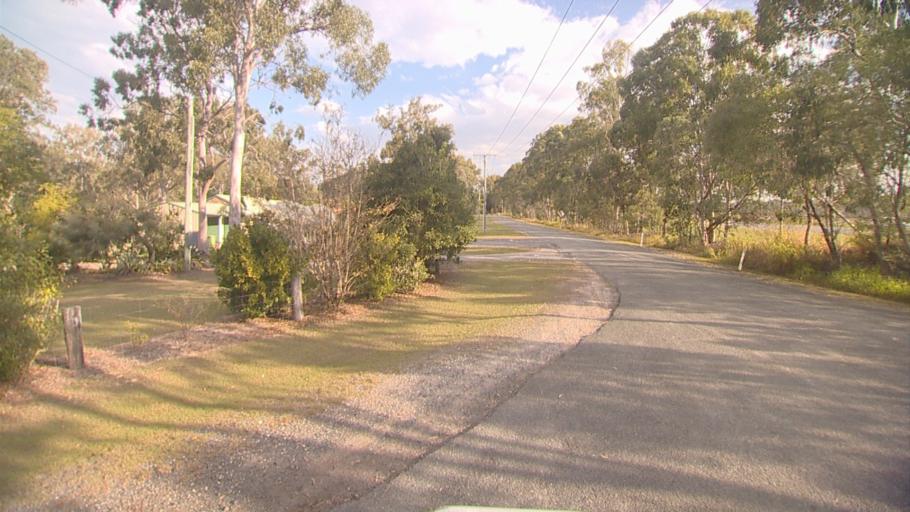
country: AU
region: Queensland
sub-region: Logan
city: Chambers Flat
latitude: -27.7749
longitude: 153.1043
